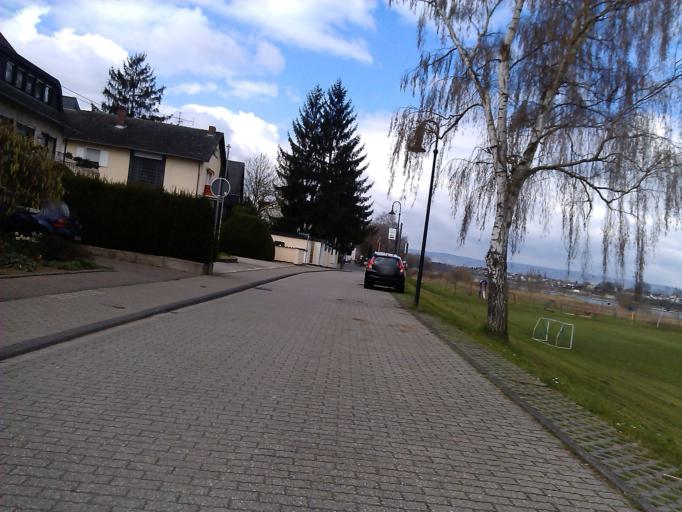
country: DE
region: Rheinland-Pfalz
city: Kaltenengers
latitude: 50.4163
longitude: 7.5481
